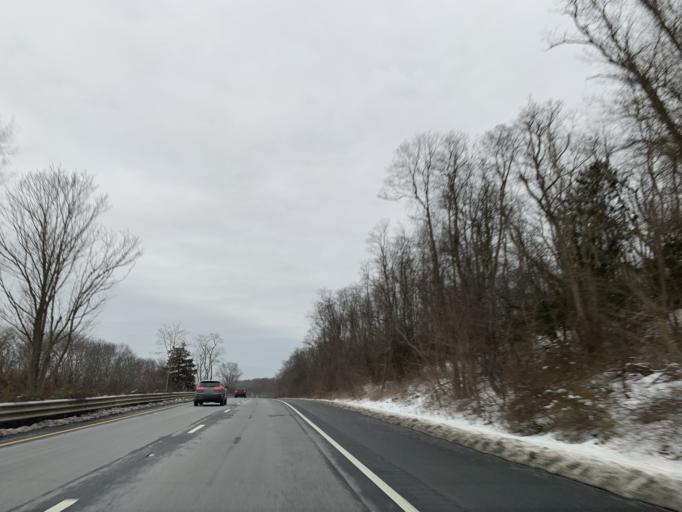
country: US
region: Massachusetts
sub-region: Bristol County
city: Somerset
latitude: 41.7363
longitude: -71.1292
